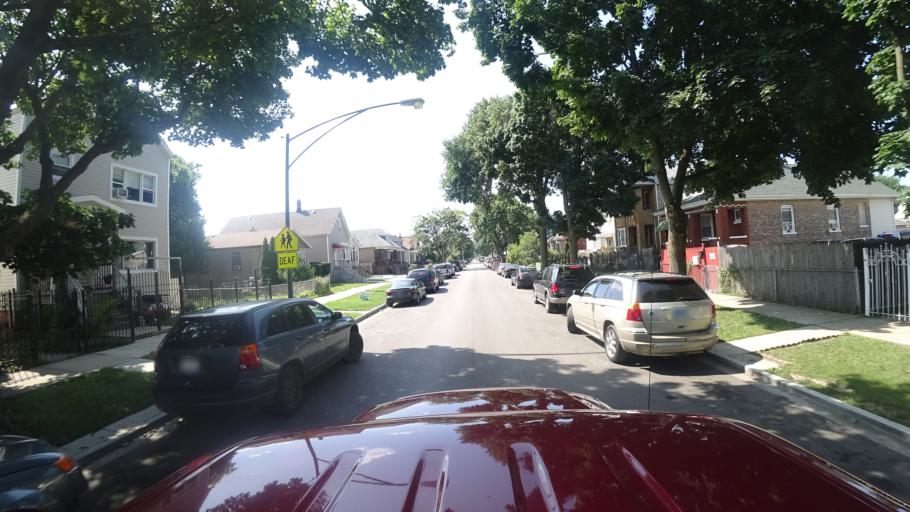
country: US
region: Illinois
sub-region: Cook County
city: Chicago
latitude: 41.7989
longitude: -87.6915
